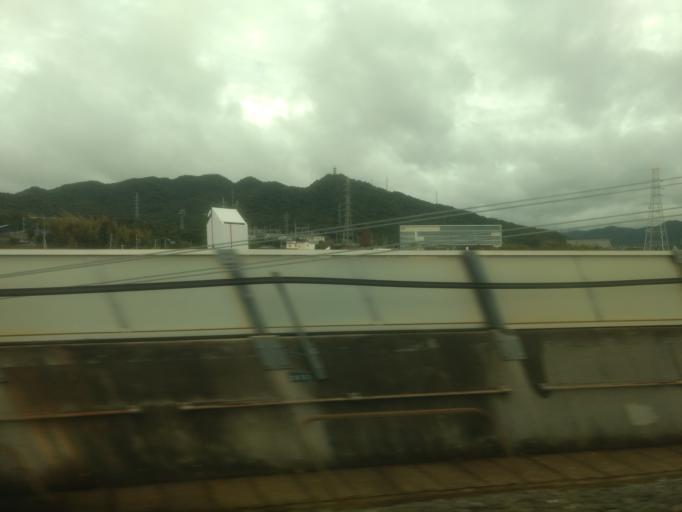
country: JP
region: Yamaguchi
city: Ogori-shimogo
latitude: 34.0887
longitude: 131.3899
